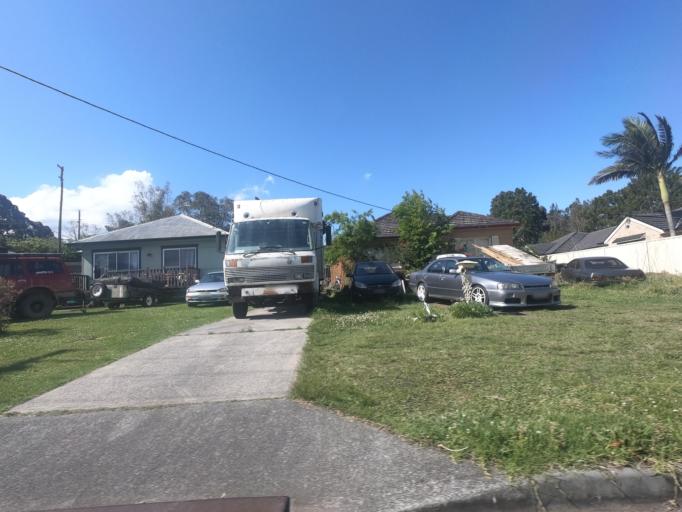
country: AU
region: New South Wales
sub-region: Wollongong
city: Cordeaux Heights
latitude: -34.4475
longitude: 150.8478
